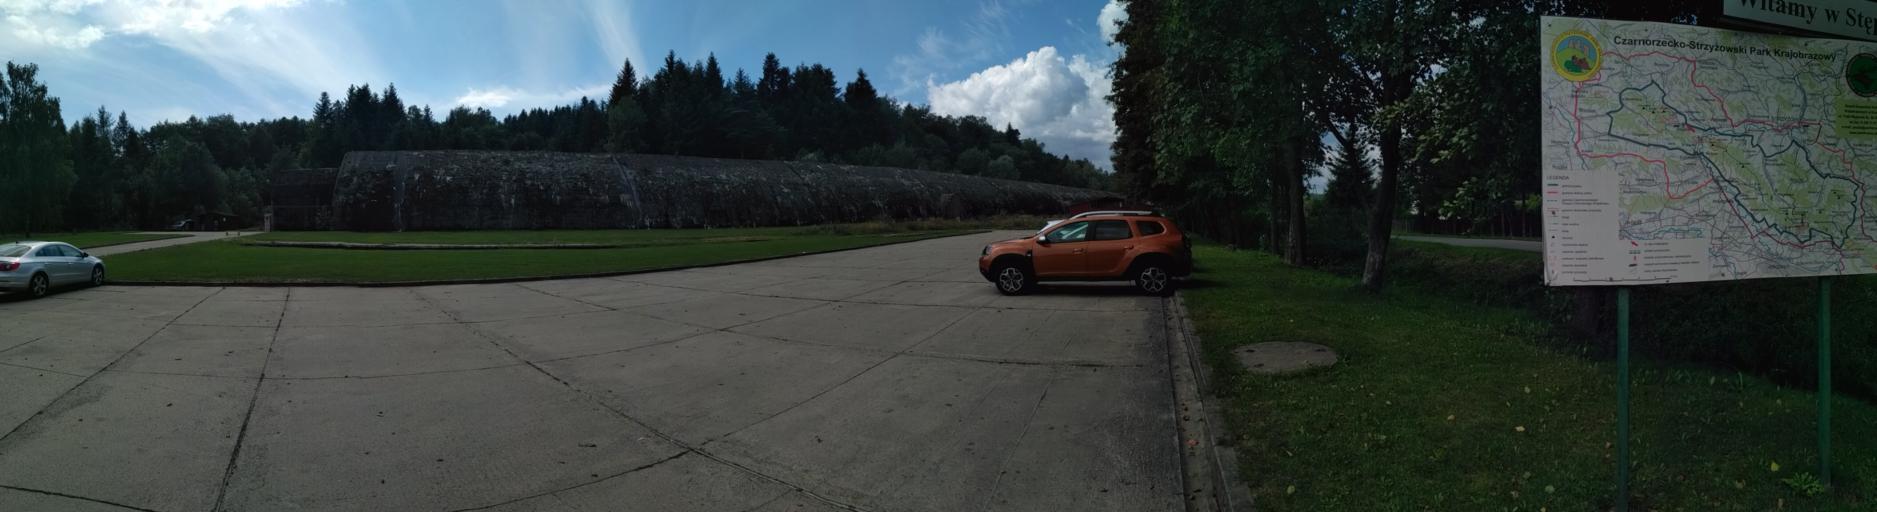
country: PL
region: Subcarpathian Voivodeship
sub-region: Powiat strzyzowski
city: Frysztak
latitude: 49.8722
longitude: 21.5916
